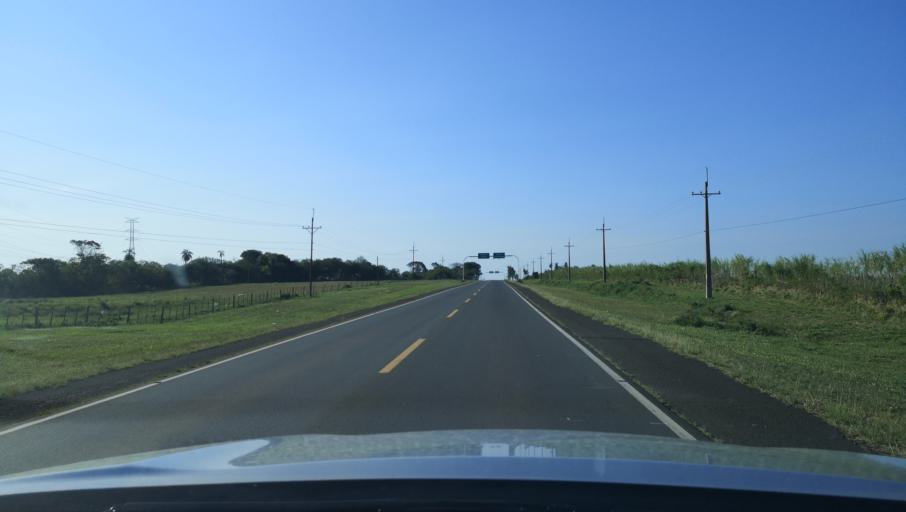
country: PY
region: Misiones
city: Santa Maria
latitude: -26.7865
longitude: -57.0259
